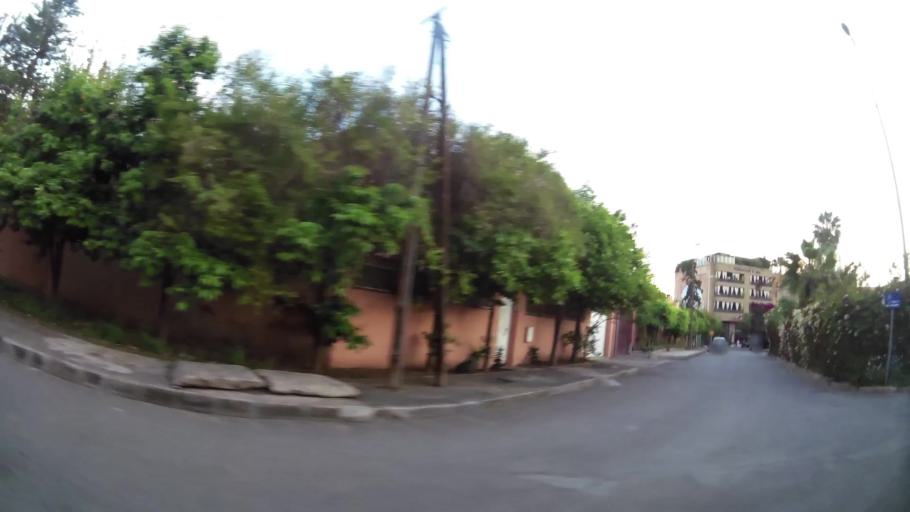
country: MA
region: Marrakech-Tensift-Al Haouz
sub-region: Marrakech
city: Marrakesh
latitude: 31.6434
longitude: -8.0221
